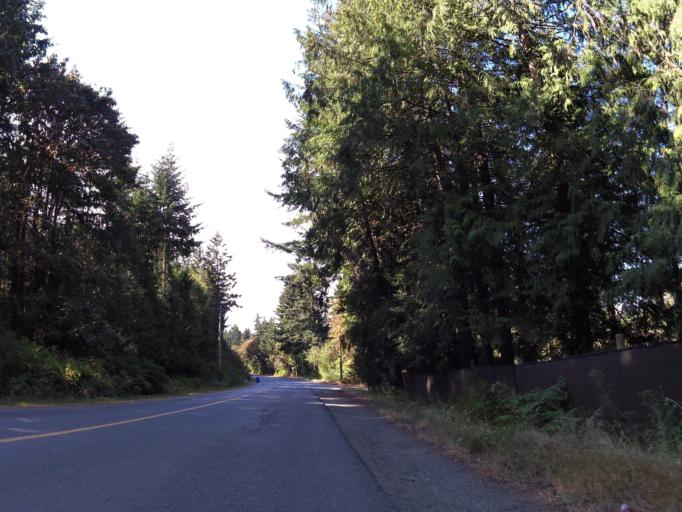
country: CA
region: British Columbia
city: North Saanich
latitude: 48.6898
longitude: -123.5567
